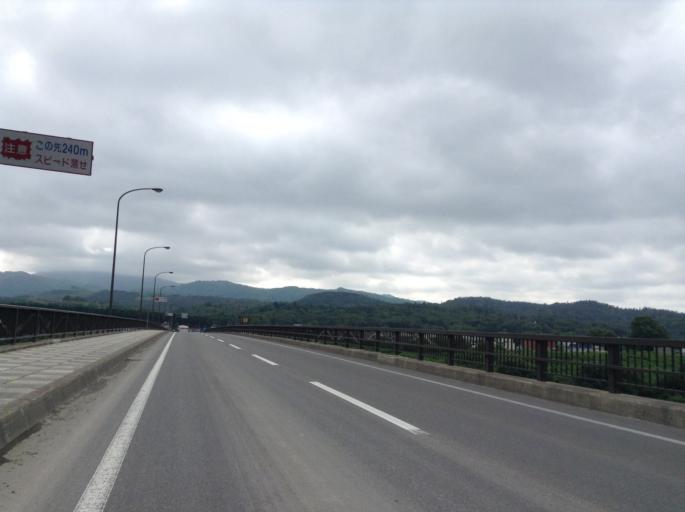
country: JP
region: Hokkaido
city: Makubetsu
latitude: 44.8185
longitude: 142.0687
